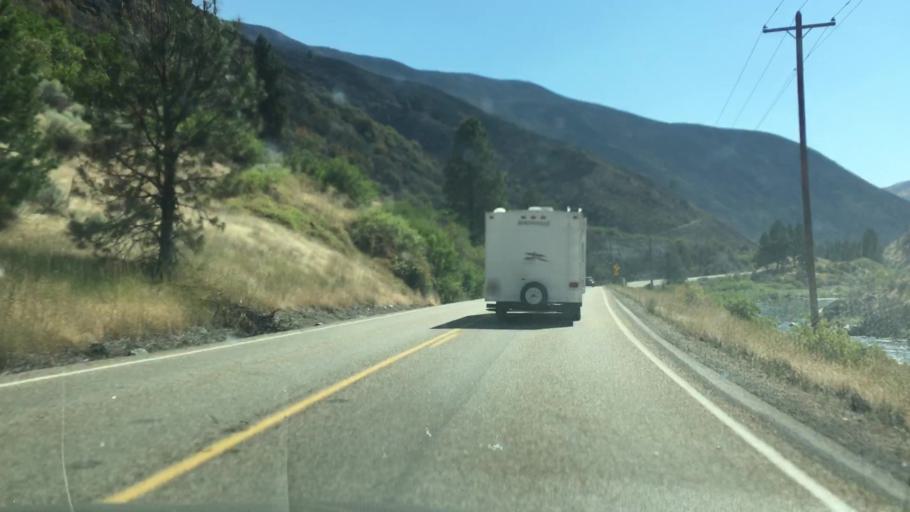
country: US
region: Idaho
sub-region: Boise County
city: Idaho City
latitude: 44.0168
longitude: -116.1524
